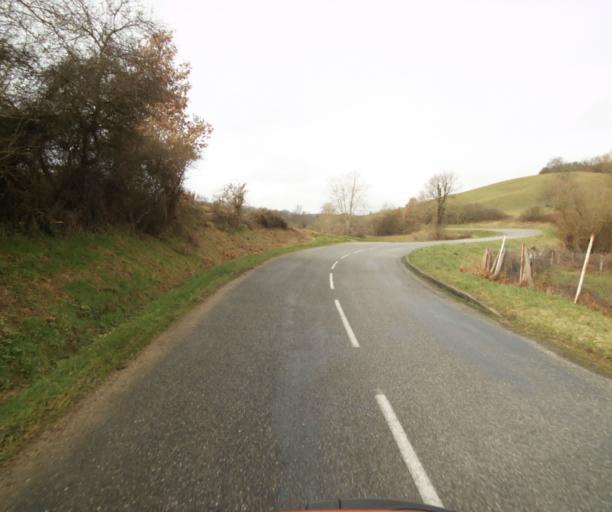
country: FR
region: Midi-Pyrenees
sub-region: Departement de l'Ariege
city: Pamiers
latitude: 43.1478
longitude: 1.5207
